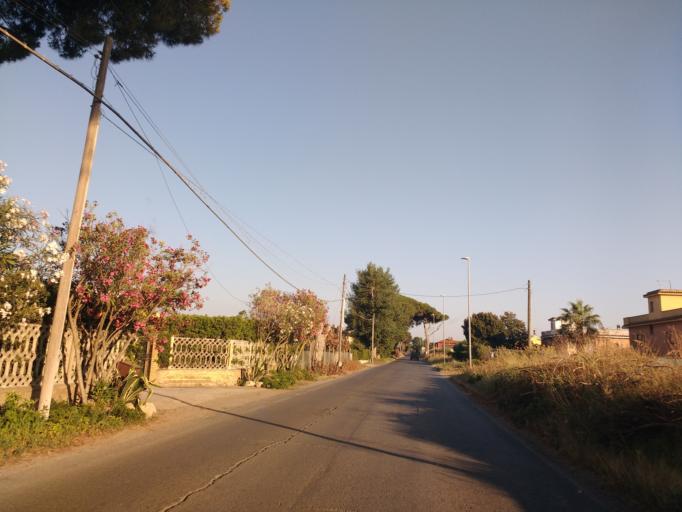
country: IT
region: Latium
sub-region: Citta metropolitana di Roma Capitale
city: Fregene
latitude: 41.8432
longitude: 12.2240
